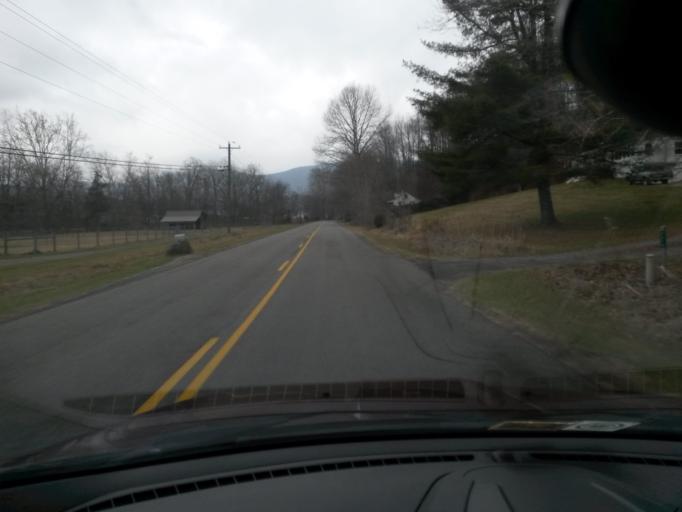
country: US
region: Virginia
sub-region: City of Lexington
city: Lexington
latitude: 37.8659
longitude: -79.5348
